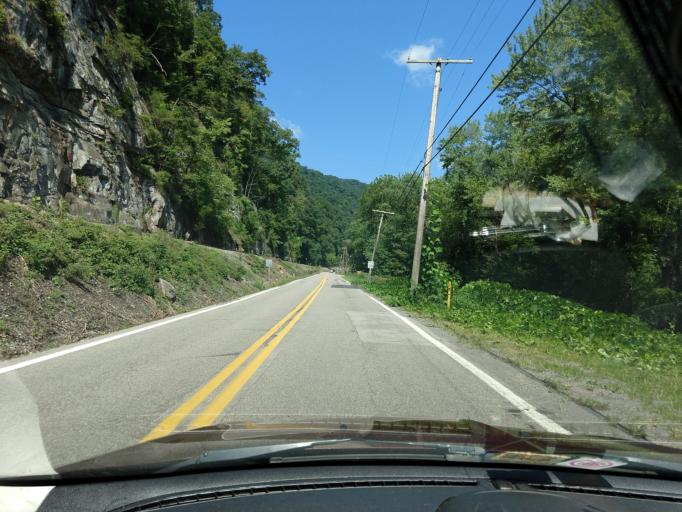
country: US
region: West Virginia
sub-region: Fayette County
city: Ansted
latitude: 38.1442
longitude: -81.2125
